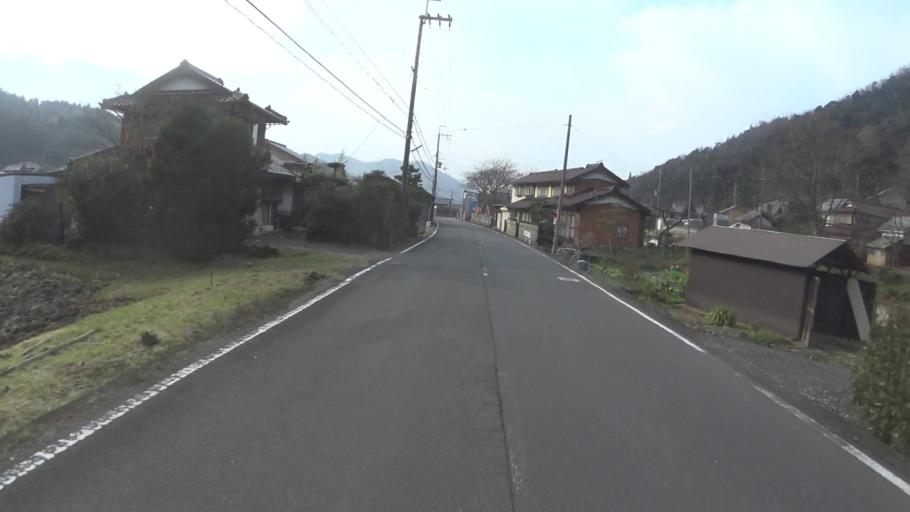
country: JP
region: Kyoto
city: Maizuru
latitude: 35.4465
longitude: 135.4264
